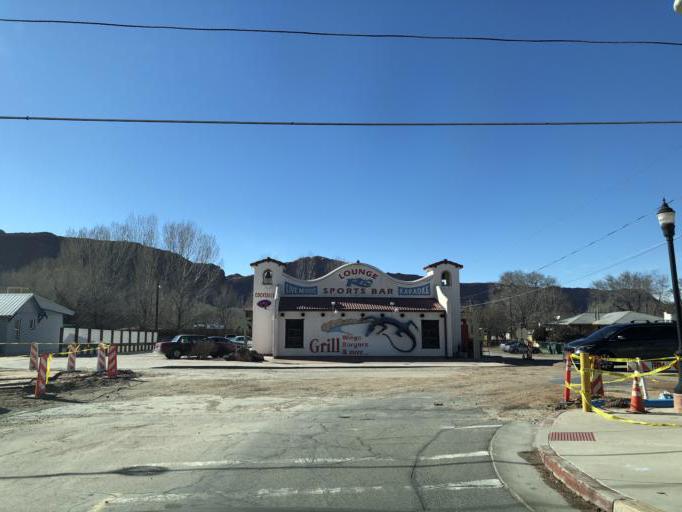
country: US
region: Utah
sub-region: Grand County
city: Moab
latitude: 38.5733
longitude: -109.5525
